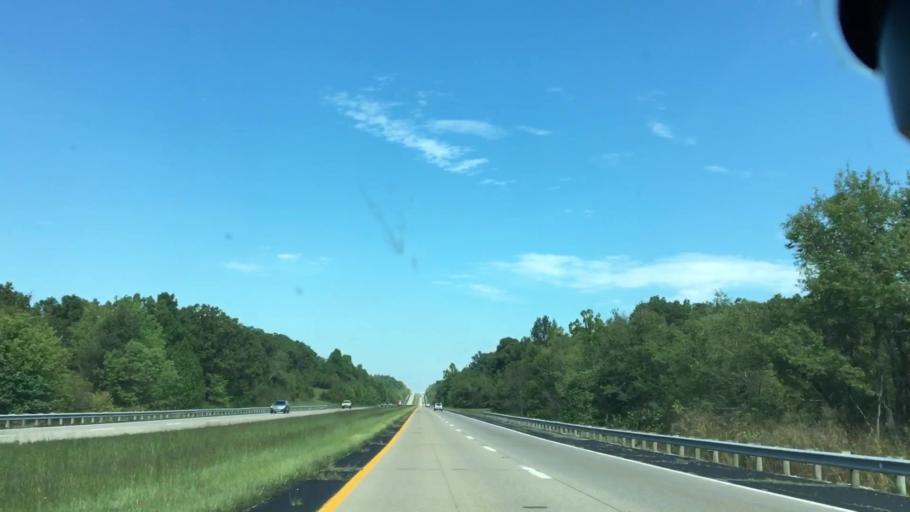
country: US
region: Kentucky
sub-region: Hopkins County
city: Nortonville
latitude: 37.0908
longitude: -87.4624
